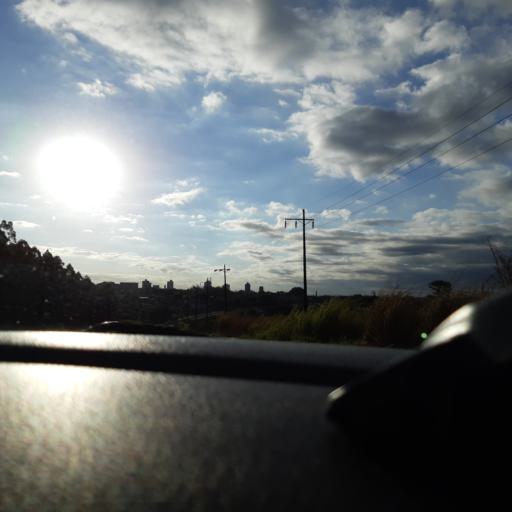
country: BR
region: Sao Paulo
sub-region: Ourinhos
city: Ourinhos
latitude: -22.9915
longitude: -49.8494
